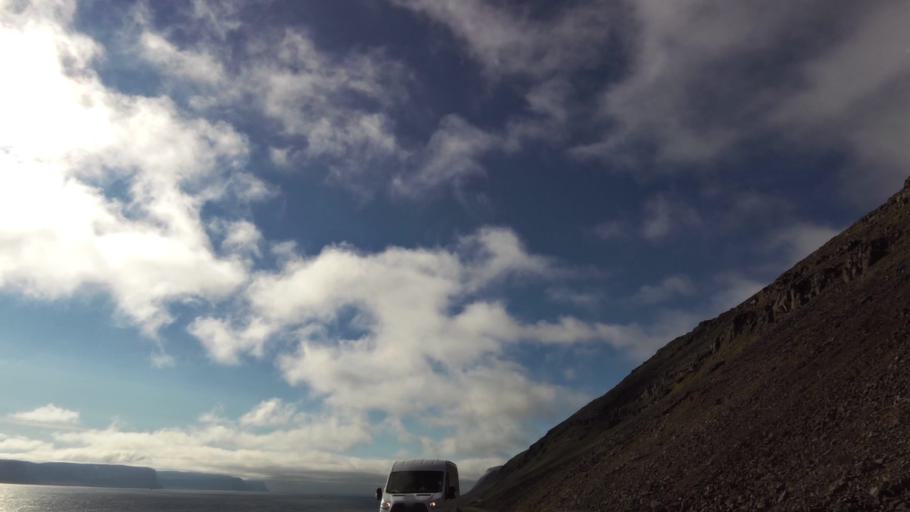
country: IS
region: West
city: Olafsvik
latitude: 65.5591
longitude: -23.9057
